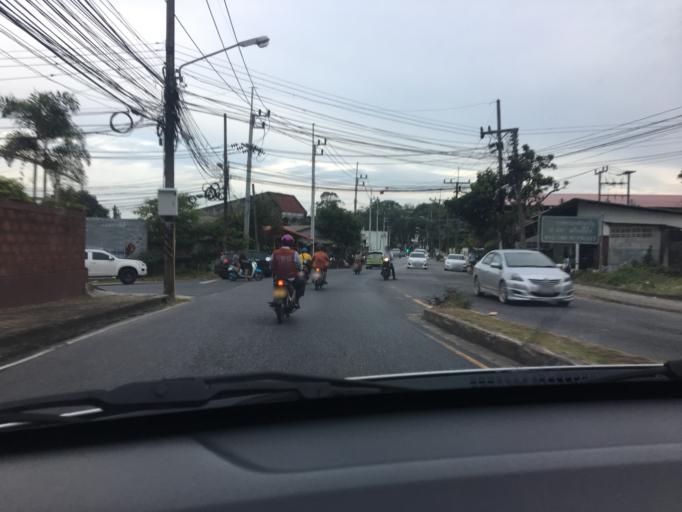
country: TH
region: Phuket
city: Phuket
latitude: 7.8972
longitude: 98.4030
